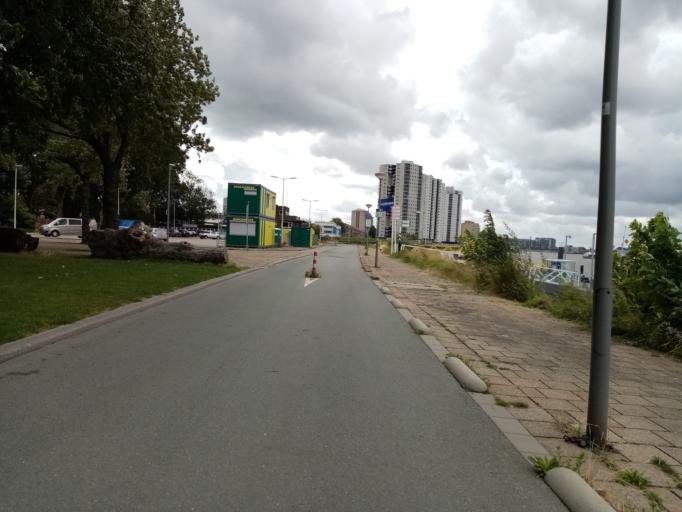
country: NL
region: South Holland
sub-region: Gemeente Rotterdam
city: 's-Gravenland
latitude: 51.9136
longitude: 4.5172
